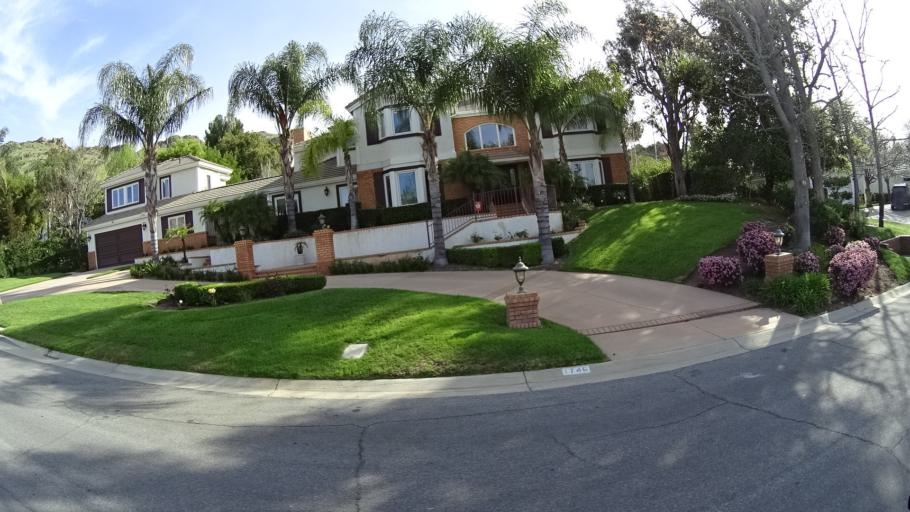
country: US
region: California
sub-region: Ventura County
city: Oak Park
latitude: 34.1954
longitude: -118.7864
